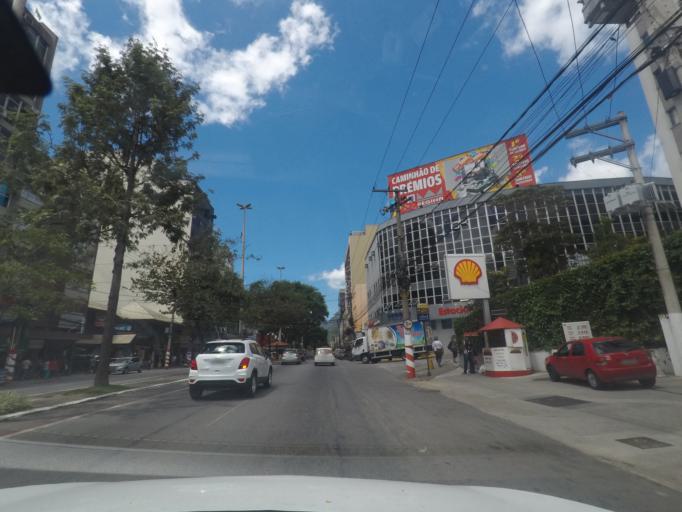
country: BR
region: Rio de Janeiro
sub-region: Teresopolis
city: Teresopolis
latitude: -22.4134
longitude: -42.9701
